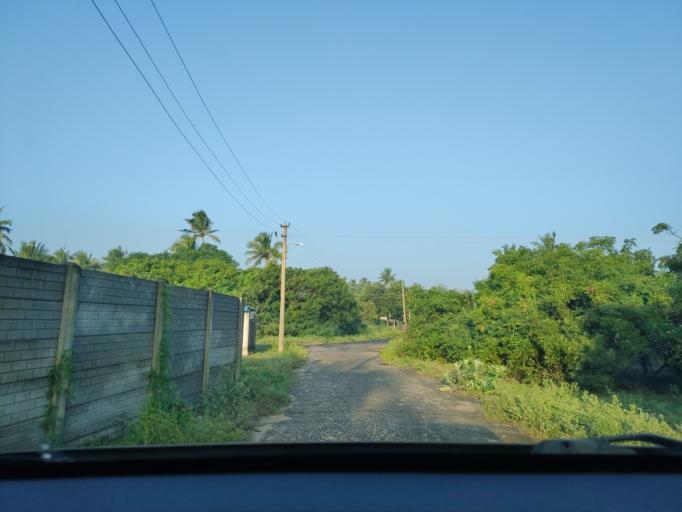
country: IN
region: Tamil Nadu
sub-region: Villupuram
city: Auroville
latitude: 12.0636
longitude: 79.8838
